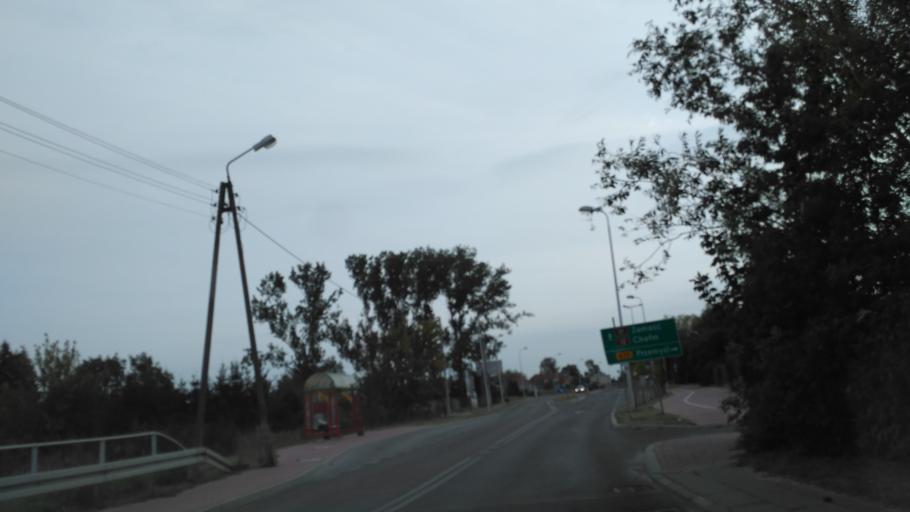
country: PL
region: Lublin Voivodeship
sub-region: Powiat lubelski
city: Lublin
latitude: 51.2075
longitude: 22.5981
